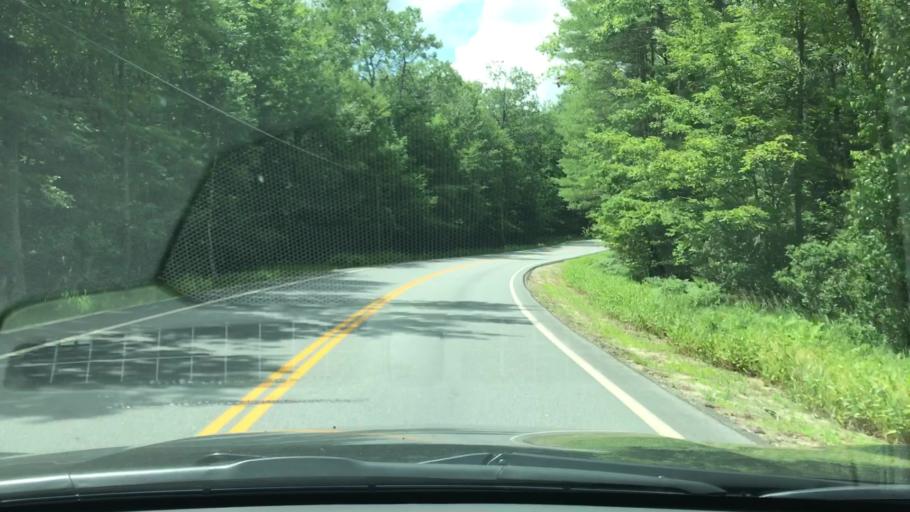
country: US
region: Maine
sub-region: Oxford County
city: Hartford
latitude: 44.3765
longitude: -70.4106
